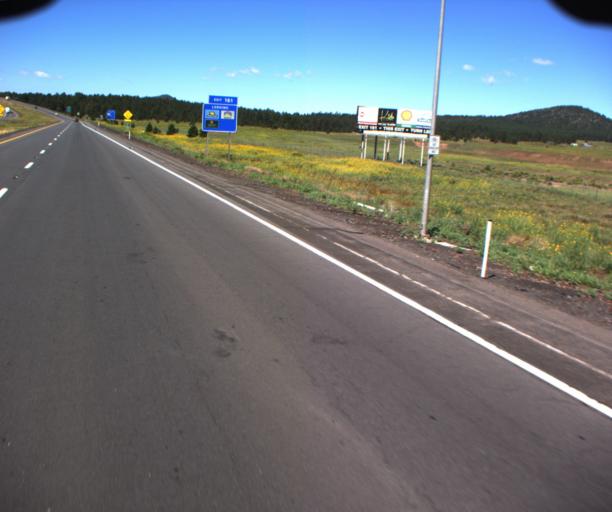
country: US
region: Arizona
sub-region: Coconino County
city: Williams
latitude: 35.2558
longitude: -112.1999
